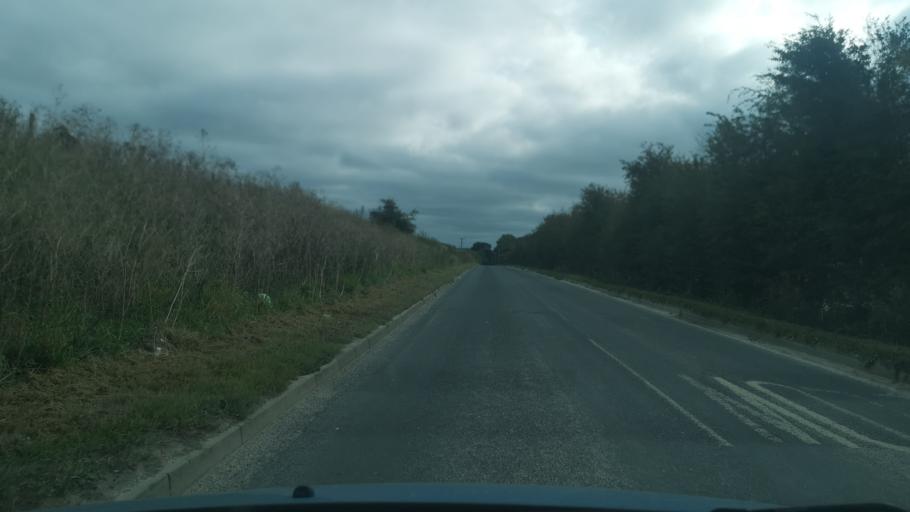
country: GB
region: England
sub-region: City and Borough of Wakefield
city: Knottingley
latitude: 53.6862
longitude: -1.2423
